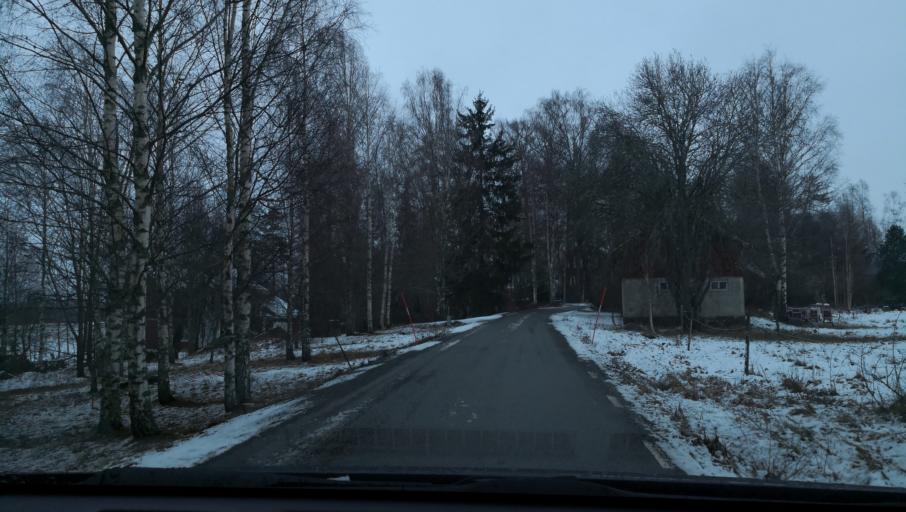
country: SE
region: Vaestmanland
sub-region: Kopings Kommun
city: Kolsva
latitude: 59.5491
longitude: 15.8796
